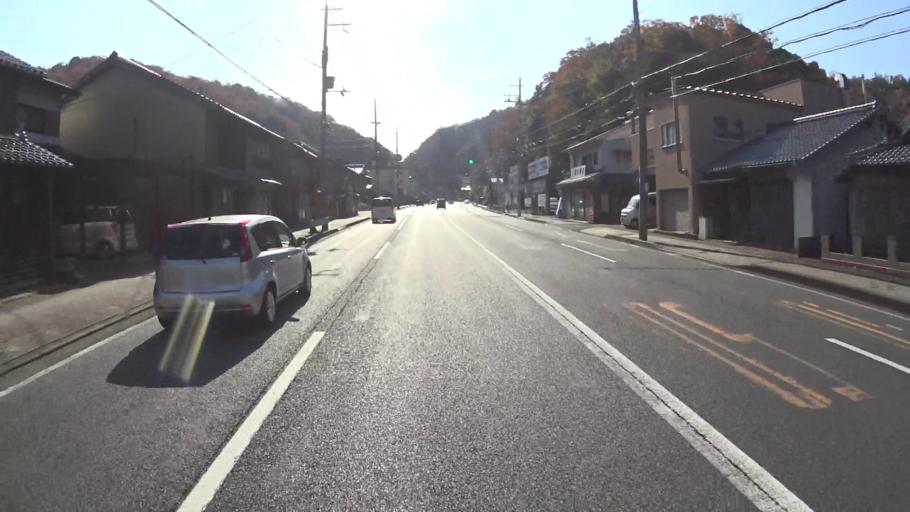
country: JP
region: Kyoto
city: Maizuru
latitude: 35.4685
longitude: 135.3648
